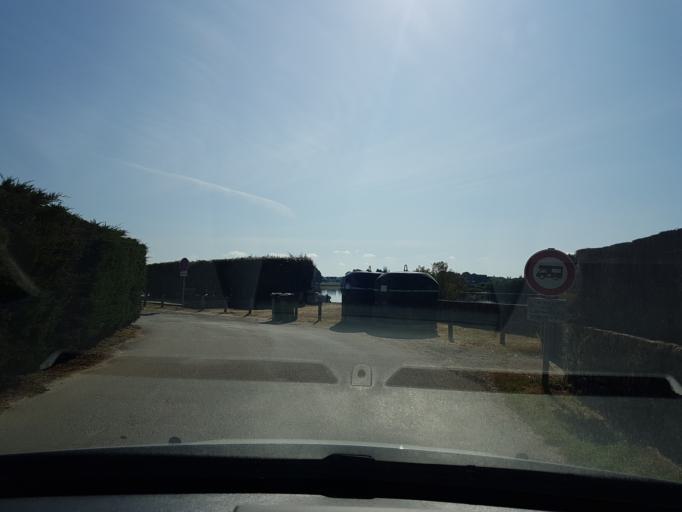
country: FR
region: Brittany
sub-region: Departement du Morbihan
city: Belz
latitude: 47.6824
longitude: -3.1842
